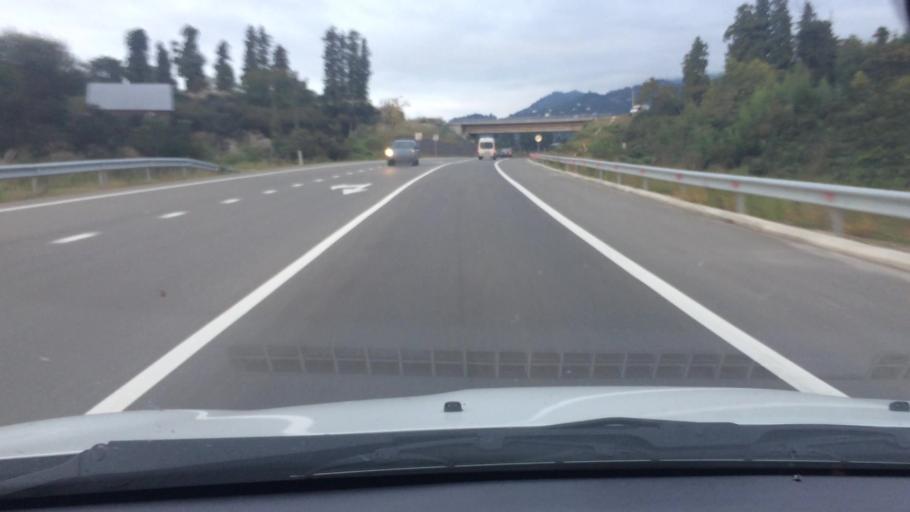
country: GE
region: Ajaria
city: Makhinjauri
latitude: 41.7056
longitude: 41.7400
